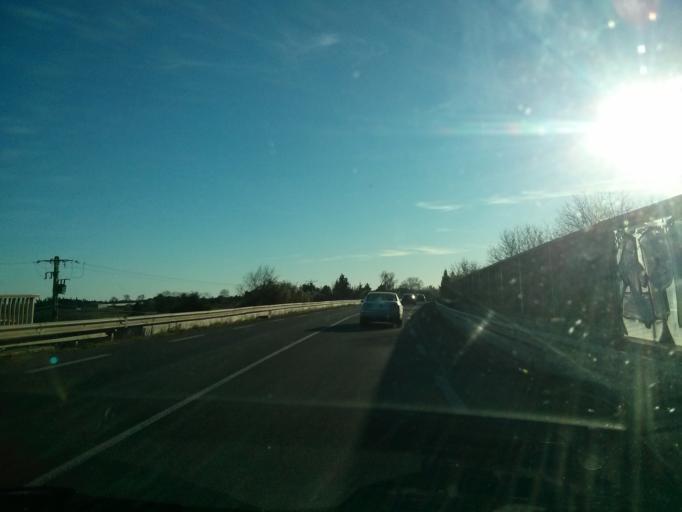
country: FR
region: Languedoc-Roussillon
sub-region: Departement de l'Herault
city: Lunel
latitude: 43.6779
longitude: 4.1507
